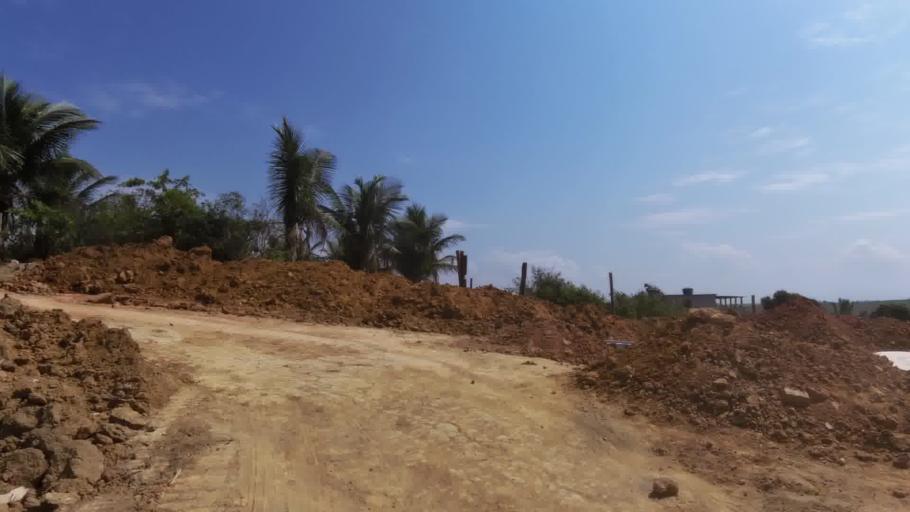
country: BR
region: Espirito Santo
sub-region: Marataizes
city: Marataizes
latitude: -21.0313
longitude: -40.8238
